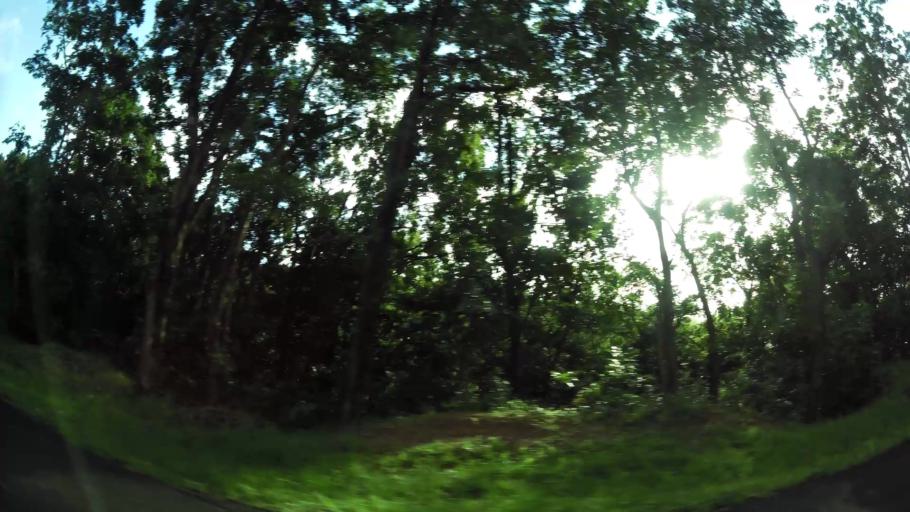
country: GP
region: Guadeloupe
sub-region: Guadeloupe
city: Bouillante
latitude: 16.1819
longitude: -61.7636
